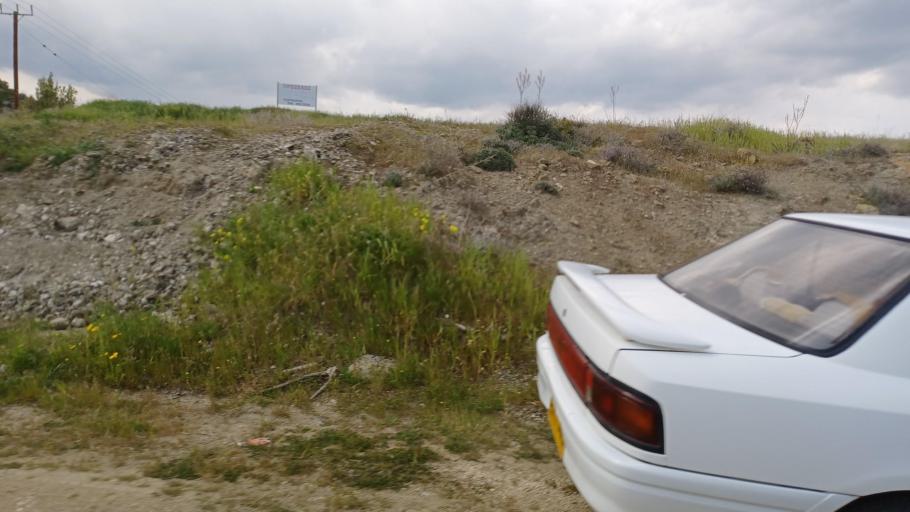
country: CY
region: Lefkosia
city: Lefka
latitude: 35.0778
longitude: 32.9092
